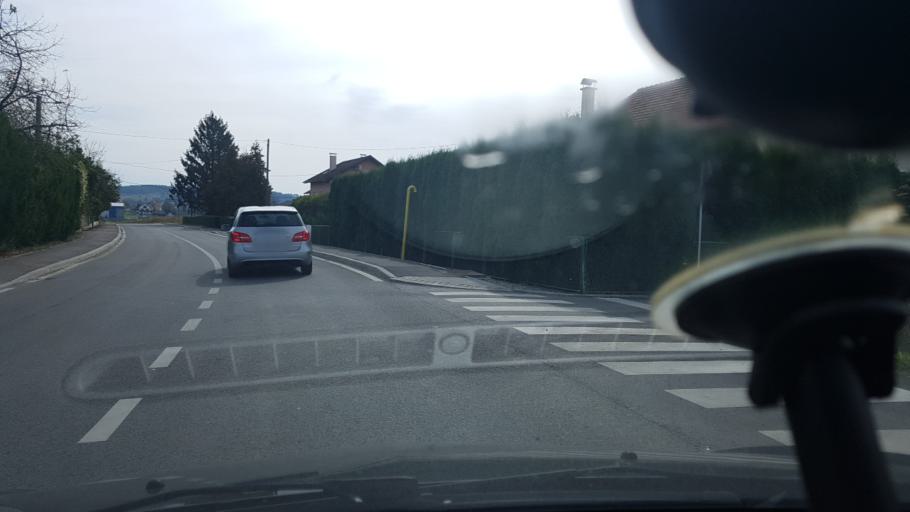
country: HR
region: Krapinsko-Zagorska
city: Marija Bistrica
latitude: 46.0536
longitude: 16.1675
